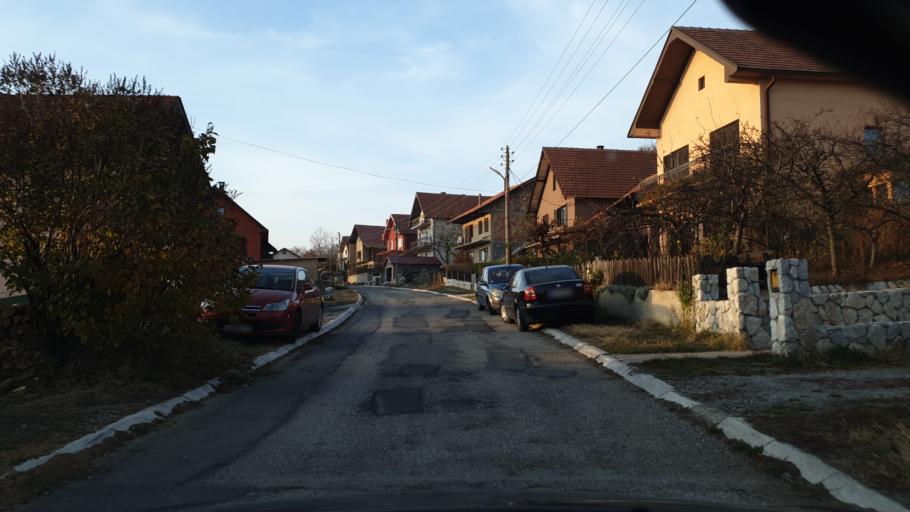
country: RS
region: Central Serbia
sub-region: Borski Okrug
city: Bor
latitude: 44.0587
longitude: 22.0832
